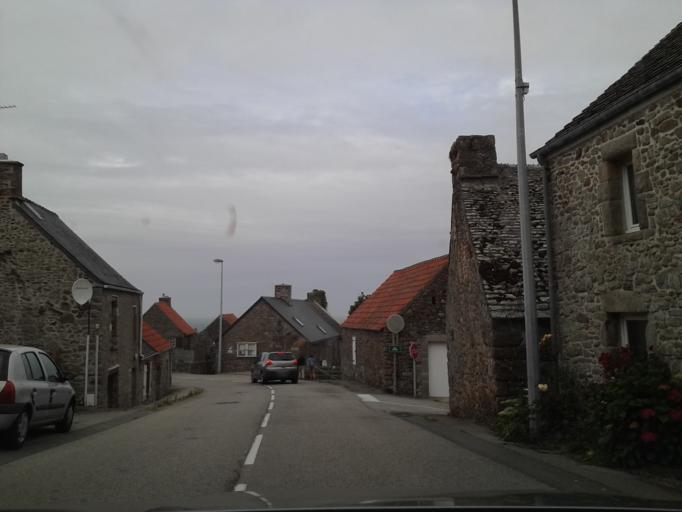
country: FR
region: Lower Normandy
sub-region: Departement de la Manche
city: Beaumont-Hague
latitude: 49.7129
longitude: -1.9308
